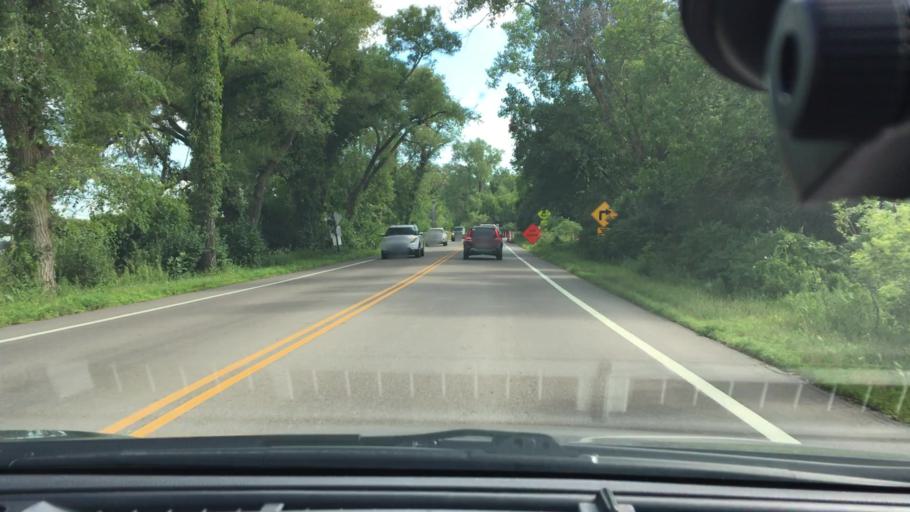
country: US
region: Minnesota
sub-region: Hennepin County
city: Long Lake
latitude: 44.9603
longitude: -93.5584
